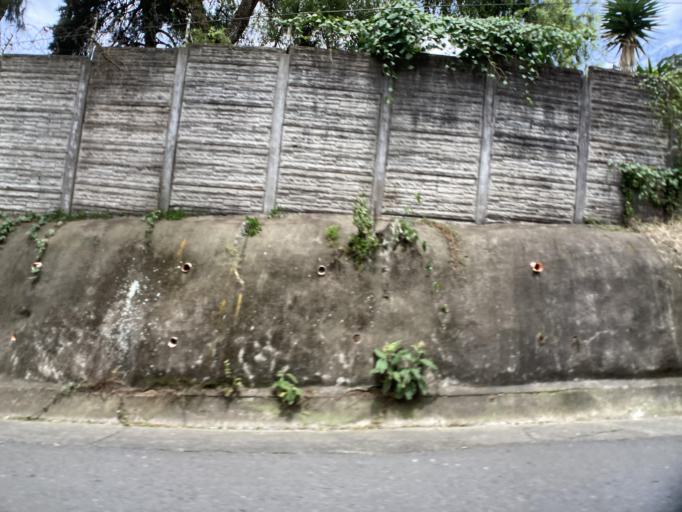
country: GT
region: Guatemala
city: Villa Canales
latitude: 14.4750
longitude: -90.4884
